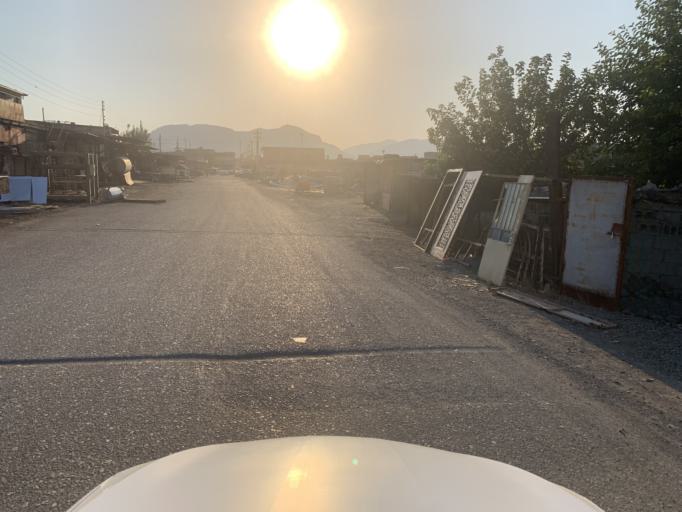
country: IQ
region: As Sulaymaniyah
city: Raniye
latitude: 36.2471
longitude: 44.8891
